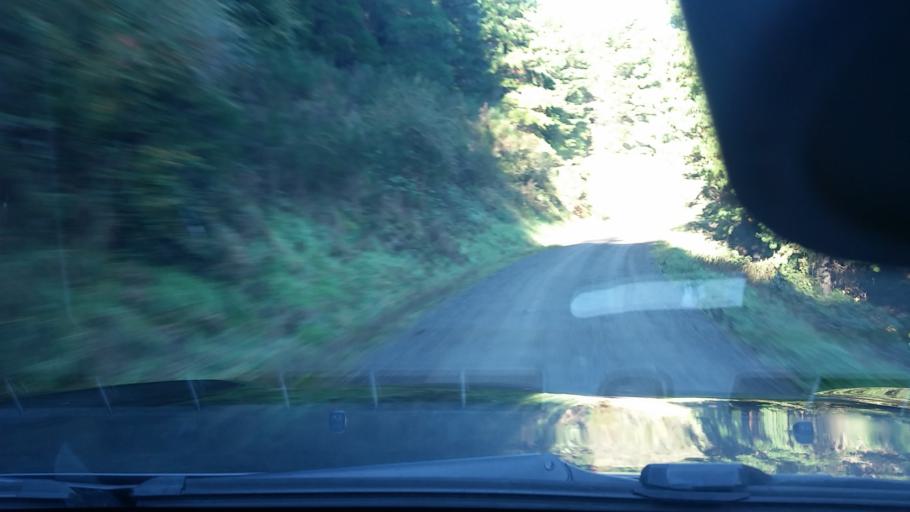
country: NZ
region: Marlborough
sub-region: Marlborough District
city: Blenheim
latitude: -41.6263
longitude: 173.9691
